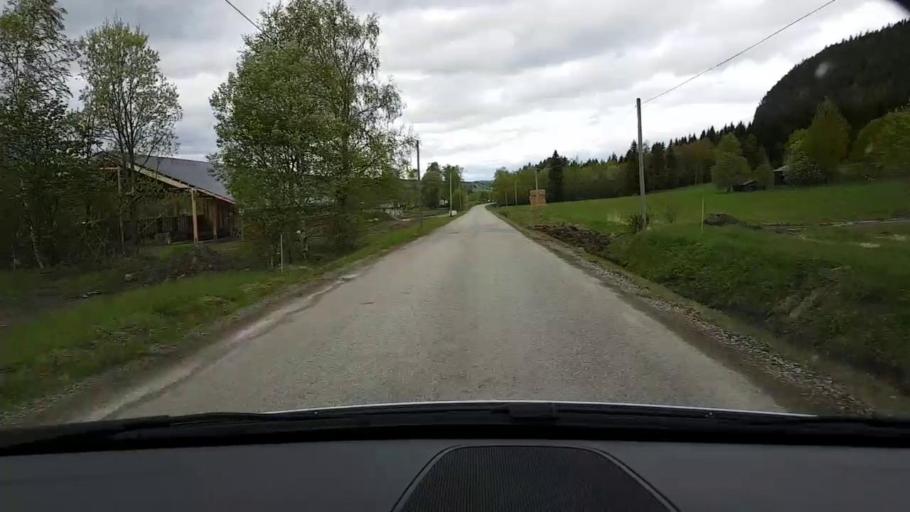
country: SE
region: Jaemtland
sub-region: Bergs Kommun
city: Hoverberg
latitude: 62.8253
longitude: 14.4228
